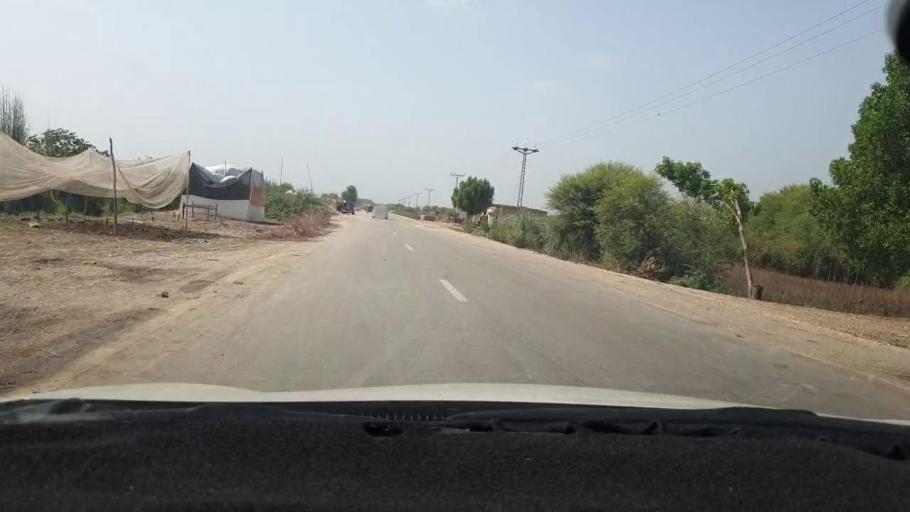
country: PK
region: Sindh
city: Mirpur Khas
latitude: 25.7043
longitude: 69.1257
